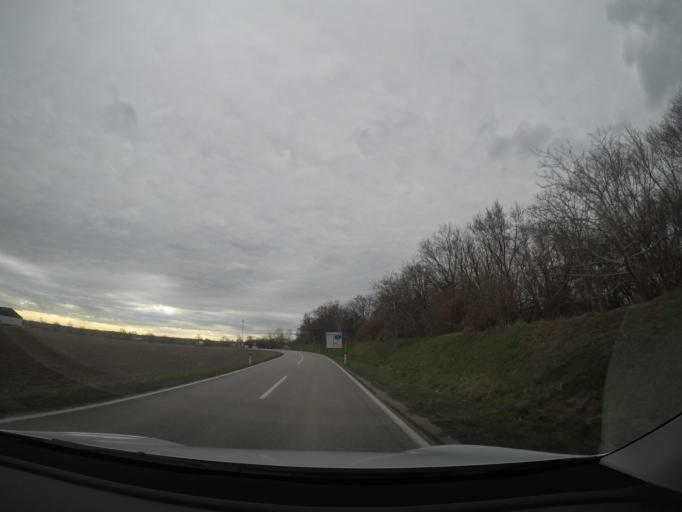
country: AT
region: Lower Austria
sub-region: Politischer Bezirk Modling
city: Biedermannsdorf
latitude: 48.0833
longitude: 16.3591
